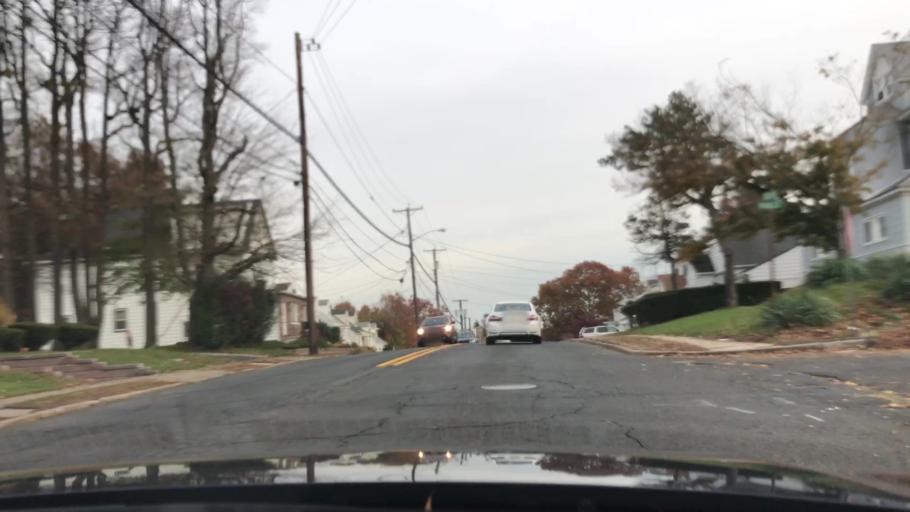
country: US
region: New Jersey
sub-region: Bergen County
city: Hasbrouck Heights
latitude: 40.8591
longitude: -74.0837
